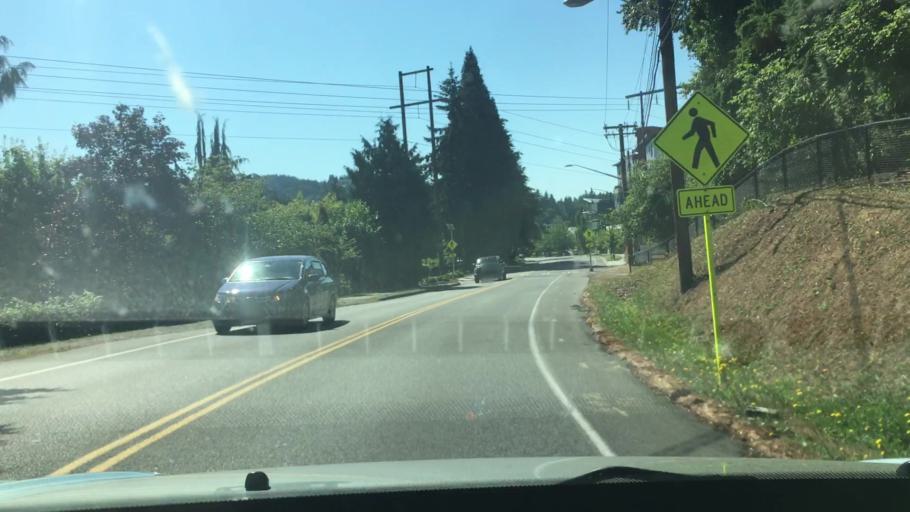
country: US
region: Washington
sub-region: King County
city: Newcastle
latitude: 47.5404
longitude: -122.1702
